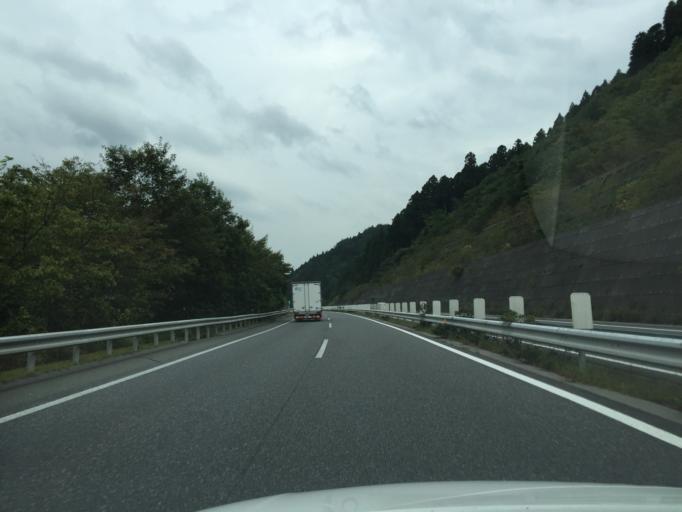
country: JP
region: Fukushima
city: Iwaki
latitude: 37.1110
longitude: 140.7554
